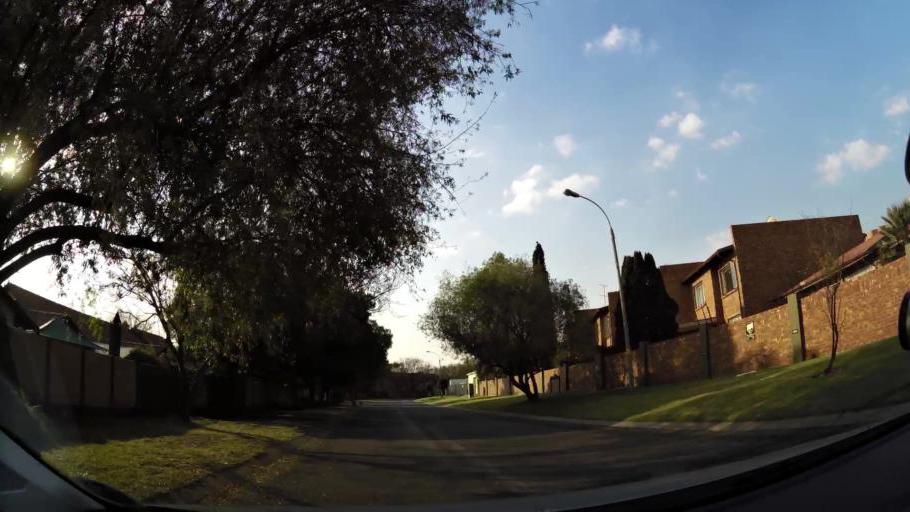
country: ZA
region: Gauteng
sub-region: City of Johannesburg Metropolitan Municipality
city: Modderfontein
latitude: -26.1312
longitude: 28.1972
